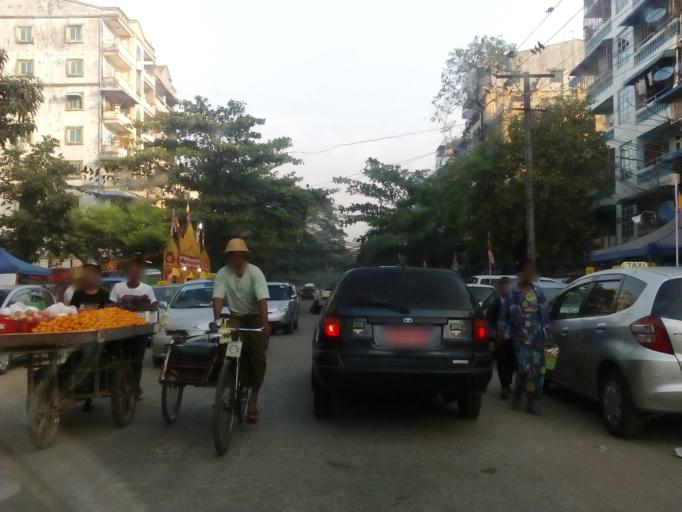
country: MM
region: Yangon
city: Yangon
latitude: 16.8035
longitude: 96.1789
